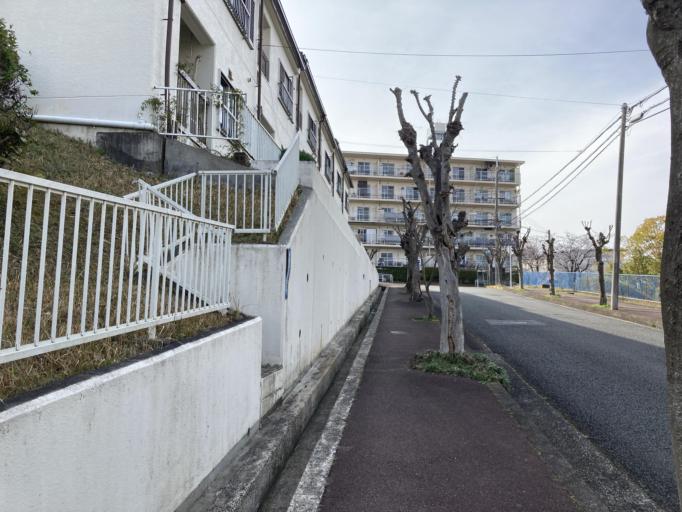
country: JP
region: Nara
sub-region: Ikoma-shi
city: Ikoma
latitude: 34.6874
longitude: 135.7252
